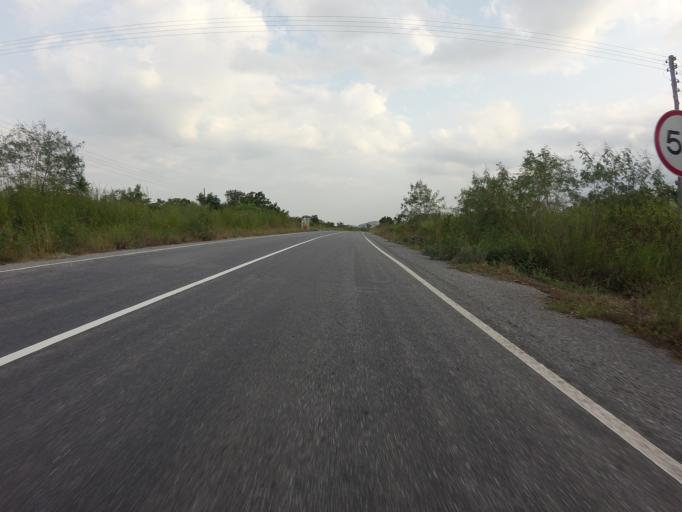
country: GH
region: Volta
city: Ho
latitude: 6.3513
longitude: 0.5376
